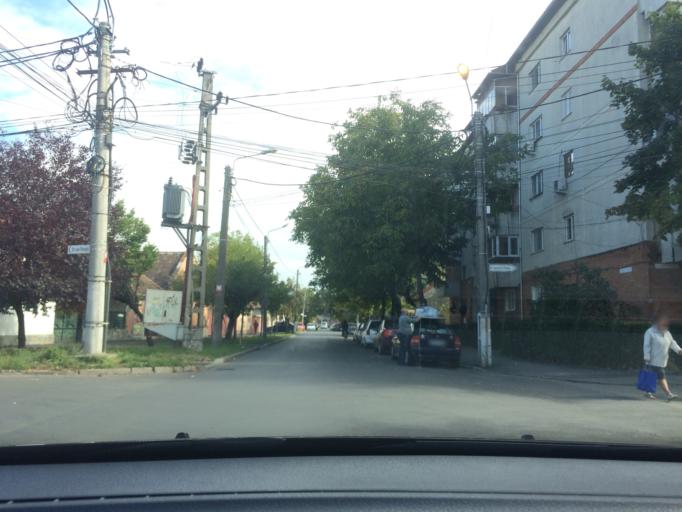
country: RO
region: Timis
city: Timisoara
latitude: 45.7620
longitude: 21.2067
